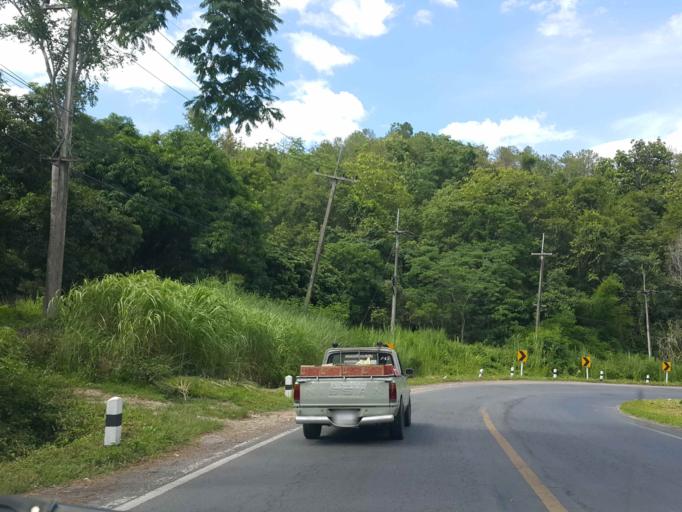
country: TH
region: Chiang Mai
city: Chiang Mai
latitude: 18.9081
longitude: 98.8899
